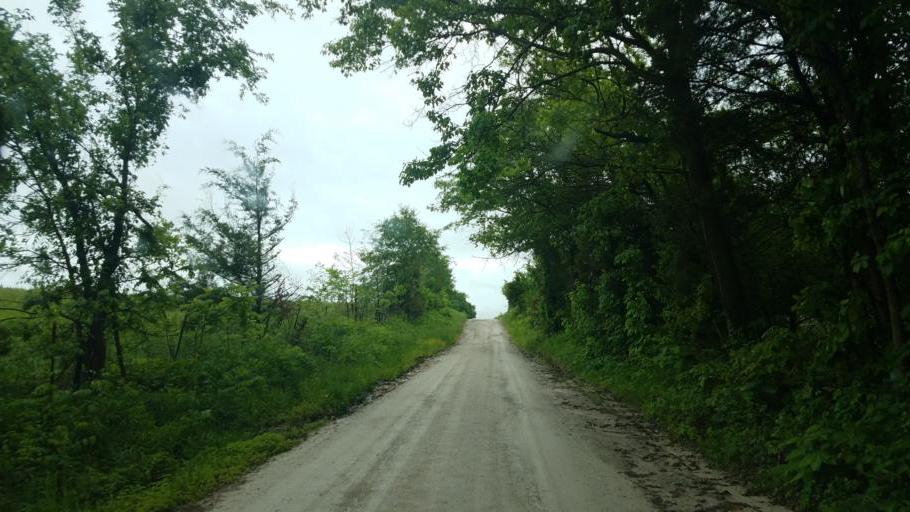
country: US
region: Missouri
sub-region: Cooper County
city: Boonville
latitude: 38.8505
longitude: -92.6405
